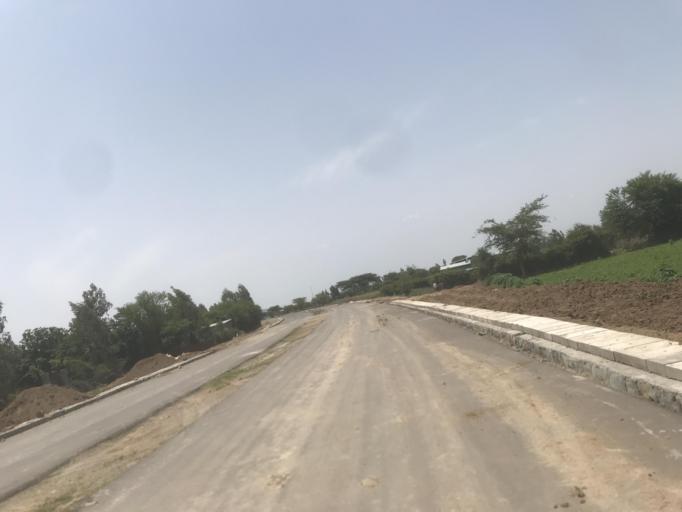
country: ET
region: Oromiya
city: Mojo
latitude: 8.2962
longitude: 38.9398
